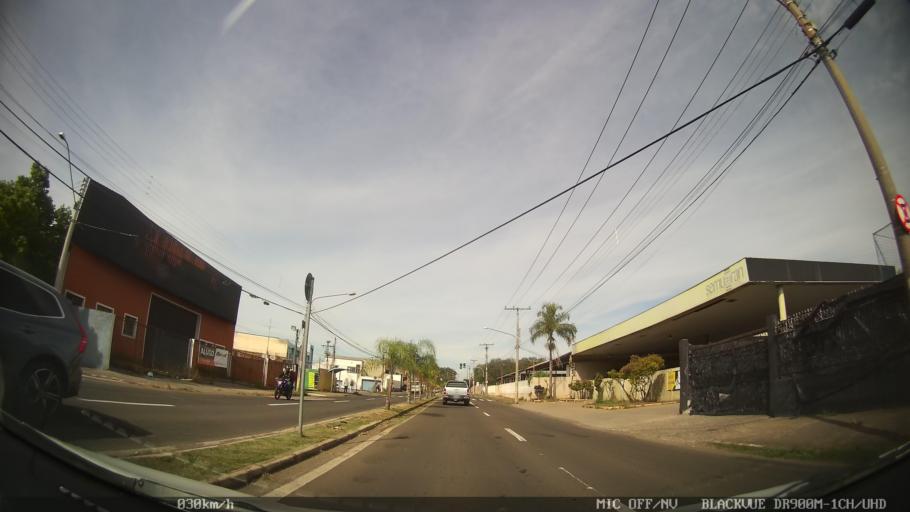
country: BR
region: Sao Paulo
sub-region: Piracicaba
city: Piracicaba
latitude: -22.7497
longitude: -47.6374
